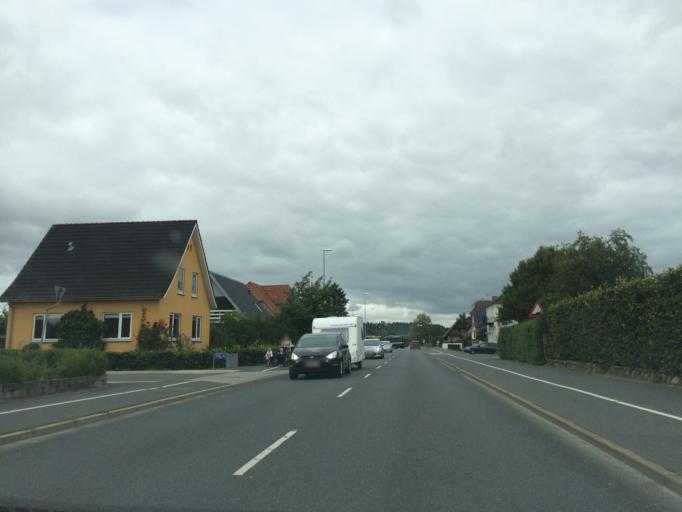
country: DK
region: Central Jutland
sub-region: Silkeborg Kommune
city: Silkeborg
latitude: 56.1790
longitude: 9.5657
